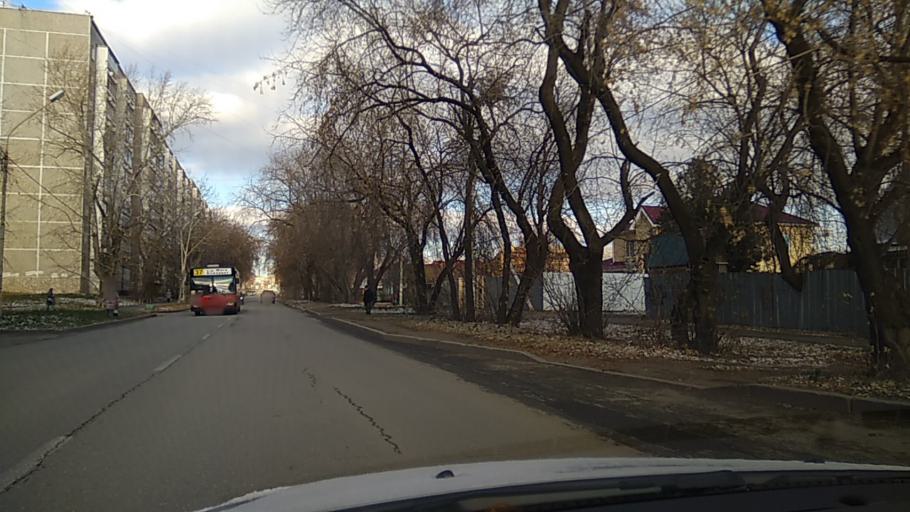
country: RU
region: Sverdlovsk
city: Sovkhoznyy
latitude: 56.7509
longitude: 60.6206
